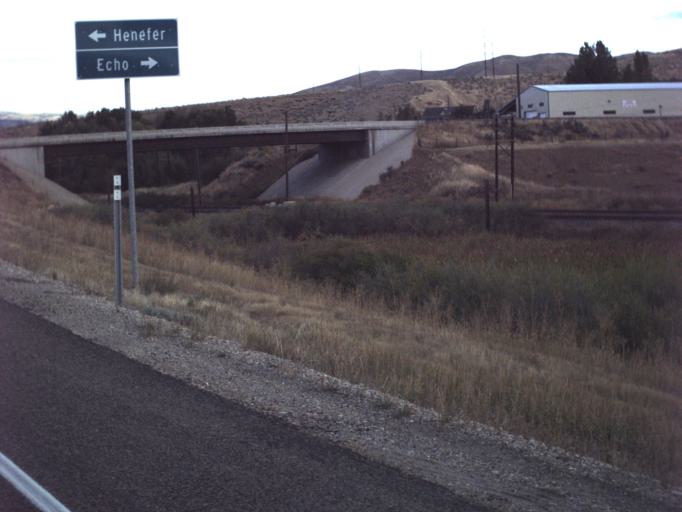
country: US
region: Utah
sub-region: Summit County
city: Coalville
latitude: 41.0149
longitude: -111.4885
